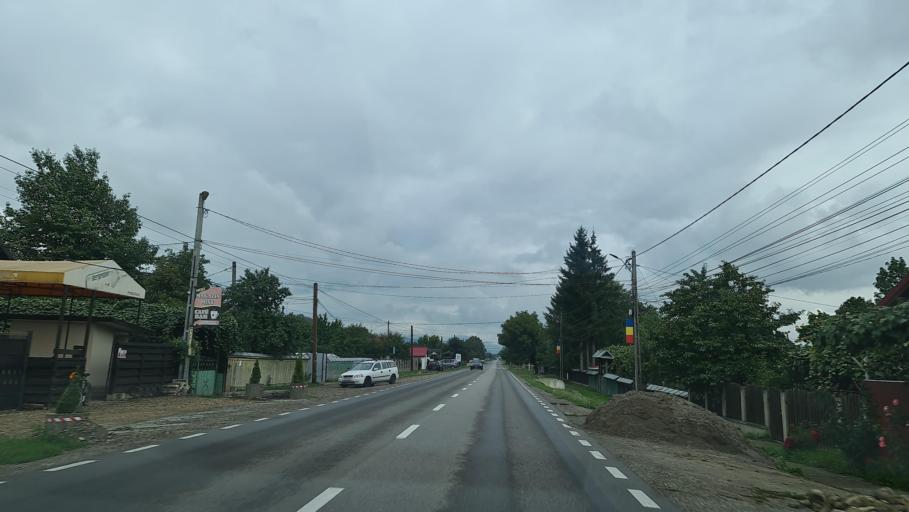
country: RO
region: Neamt
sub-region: Comuna Roznov
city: Roznov
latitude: 46.8158
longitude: 26.5095
